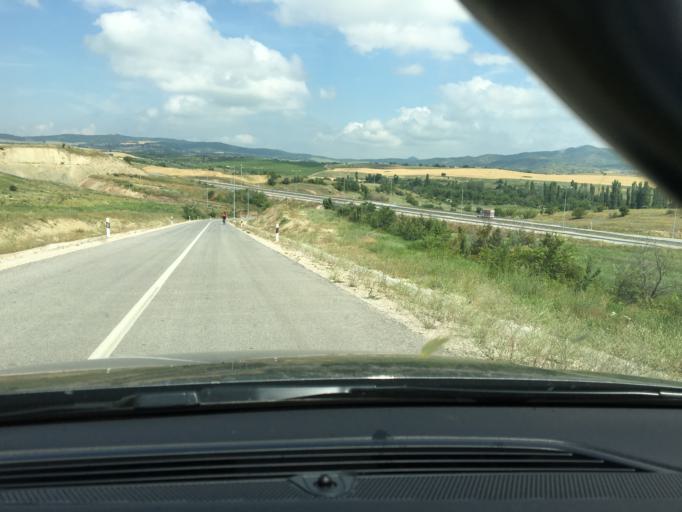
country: MK
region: Sveti Nikole
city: Gorobinci
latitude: 41.9146
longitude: 21.8799
